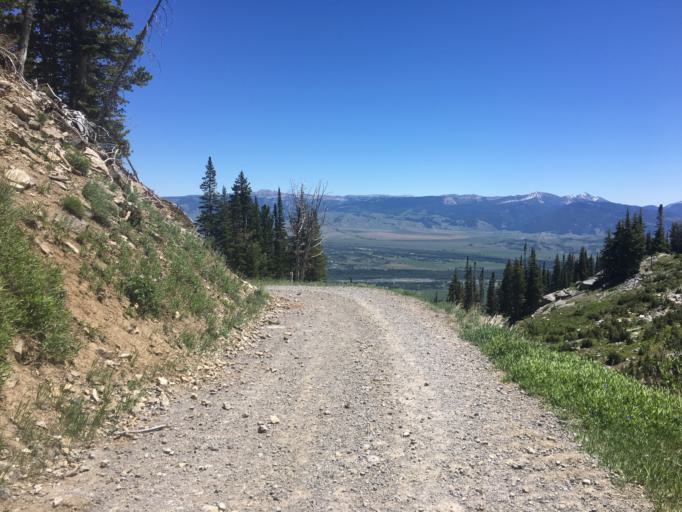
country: US
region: Wyoming
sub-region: Teton County
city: Moose Wilson Road
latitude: 43.5987
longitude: -110.8603
